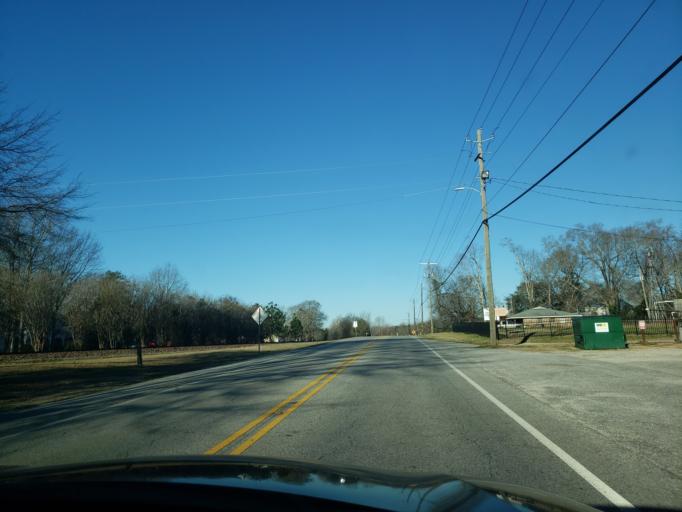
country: US
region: Alabama
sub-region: Lee County
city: Auburn
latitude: 32.6043
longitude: -85.5990
